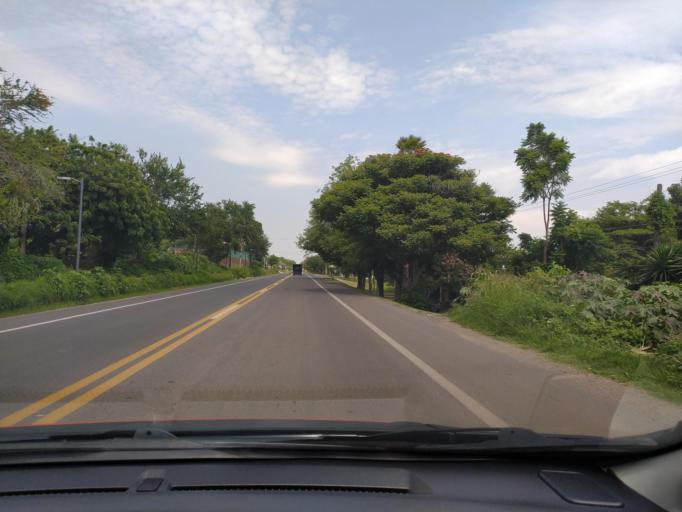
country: MX
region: Jalisco
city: San Juan Cosala
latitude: 20.2922
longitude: -103.3690
